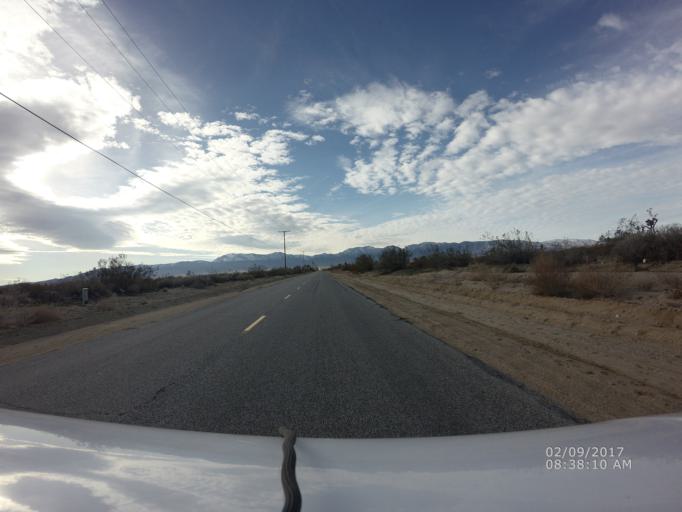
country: US
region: California
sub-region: Los Angeles County
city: Lake Los Angeles
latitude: 34.5491
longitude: -117.8356
